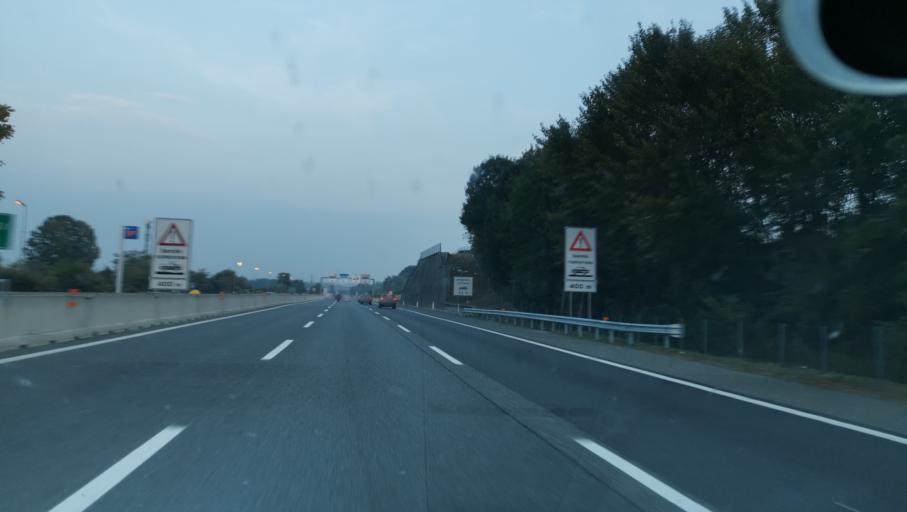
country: IT
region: Piedmont
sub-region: Provincia di Torino
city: Rivoli
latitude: 45.0842
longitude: 7.5282
